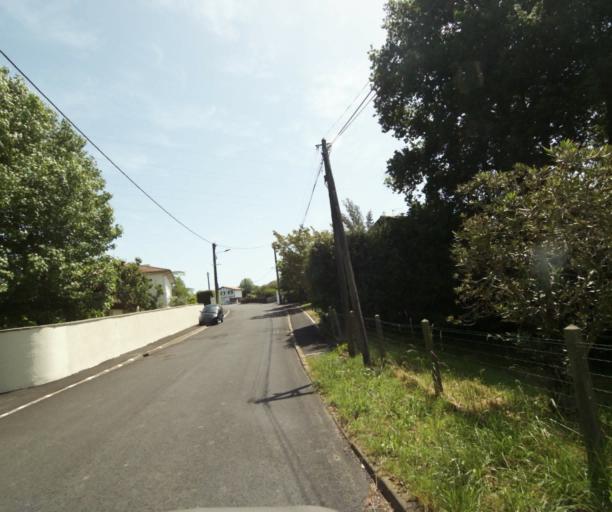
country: FR
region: Aquitaine
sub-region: Departement des Pyrenees-Atlantiques
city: Mouguerre
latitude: 43.4646
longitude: -1.4380
